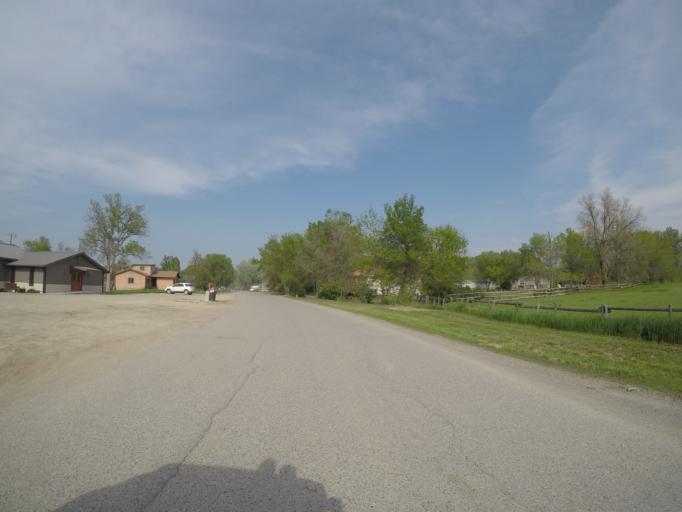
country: US
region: Montana
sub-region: Yellowstone County
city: Laurel
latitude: 45.4815
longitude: -108.9780
